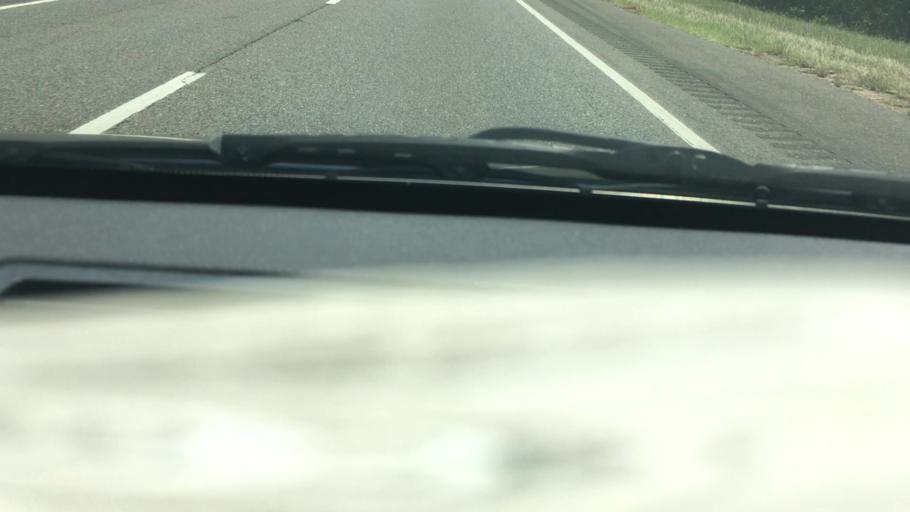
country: US
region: Alabama
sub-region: Pickens County
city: Gordo
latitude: 33.2738
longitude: -87.7570
